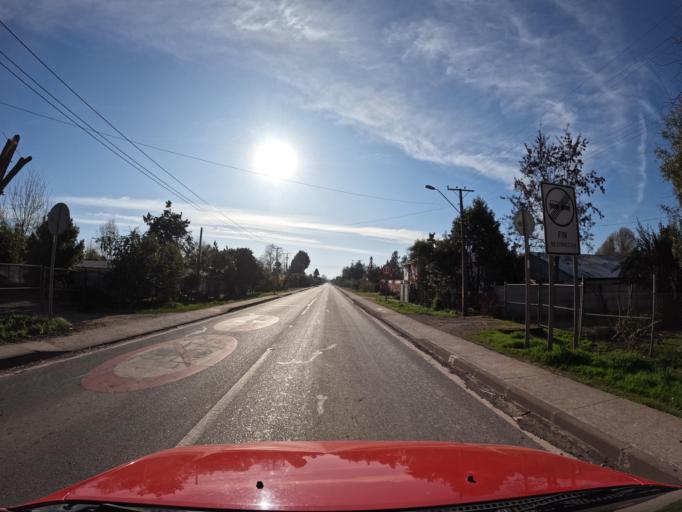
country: CL
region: Maule
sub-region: Provincia de Curico
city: Teno
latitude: -34.9582
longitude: -70.9738
